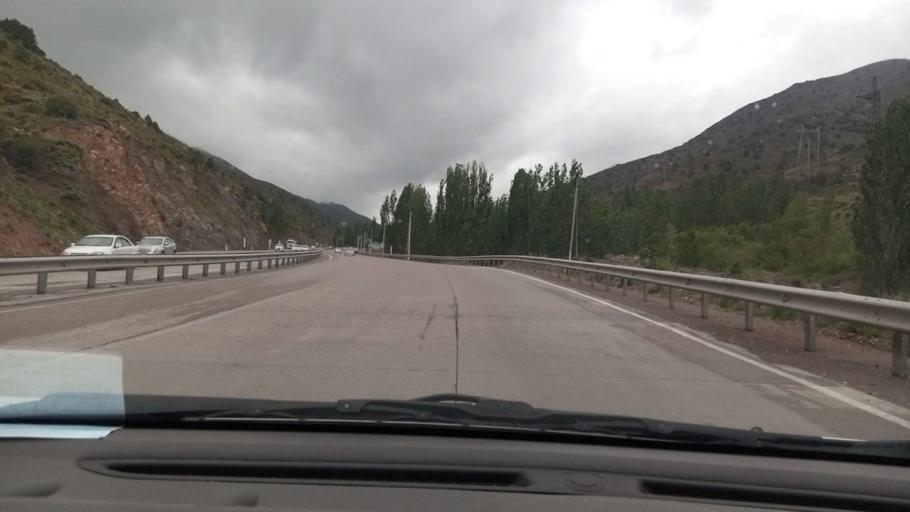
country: TJ
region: Viloyati Sughd
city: Shaydon
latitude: 41.0364
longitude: 70.5818
